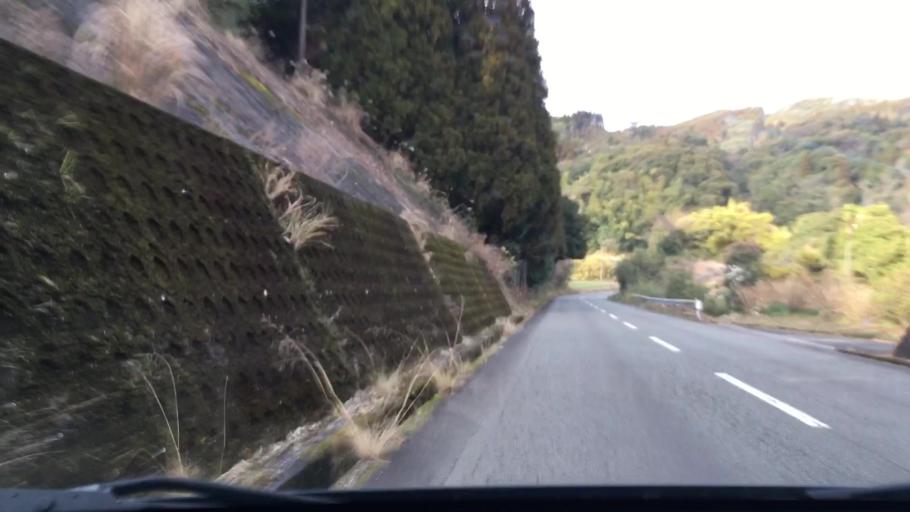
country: JP
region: Miyazaki
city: Nichinan
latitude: 31.5939
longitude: 131.3070
